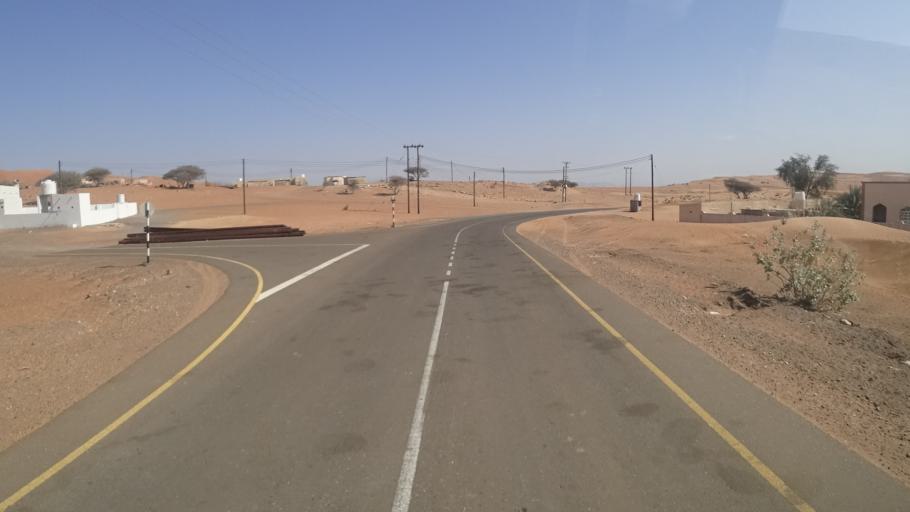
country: OM
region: Ash Sharqiyah
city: Al Qabil
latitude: 22.4848
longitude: 58.7127
